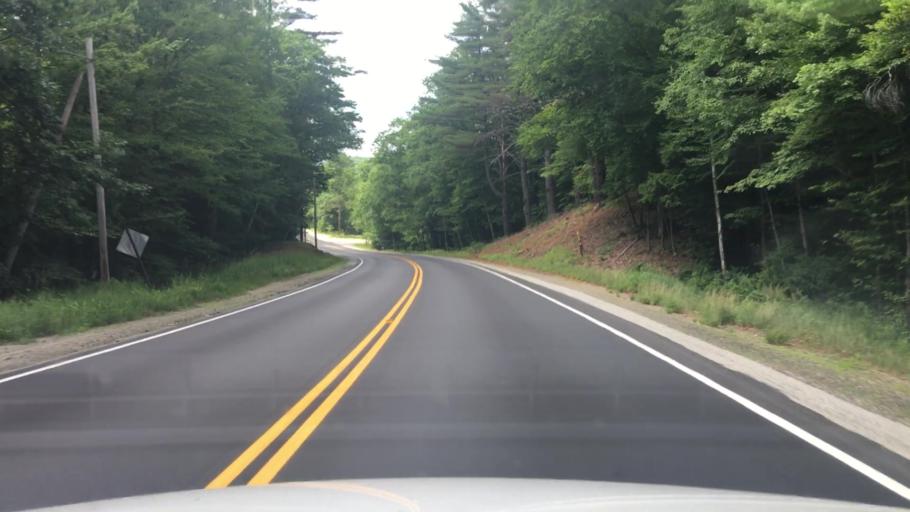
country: US
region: Maine
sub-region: Oxford County
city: West Paris
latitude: 44.3944
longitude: -70.6633
